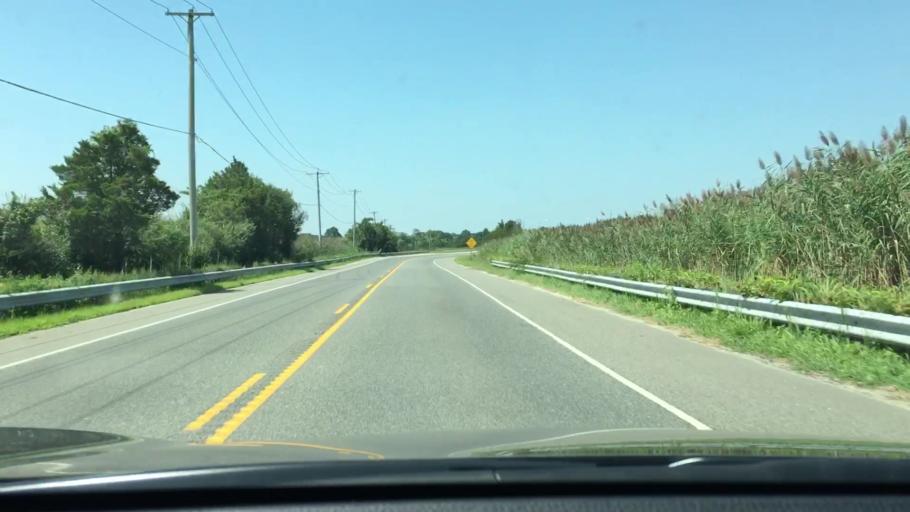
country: US
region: New Jersey
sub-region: Cumberland County
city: Port Norris
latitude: 39.2871
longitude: -74.9837
